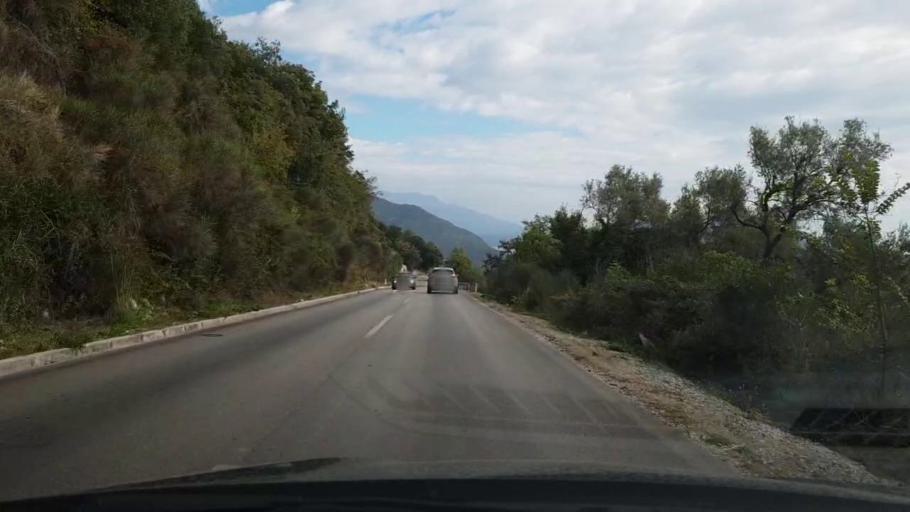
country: ME
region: Herceg Novi
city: Herceg-Novi
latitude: 42.4692
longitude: 18.5403
